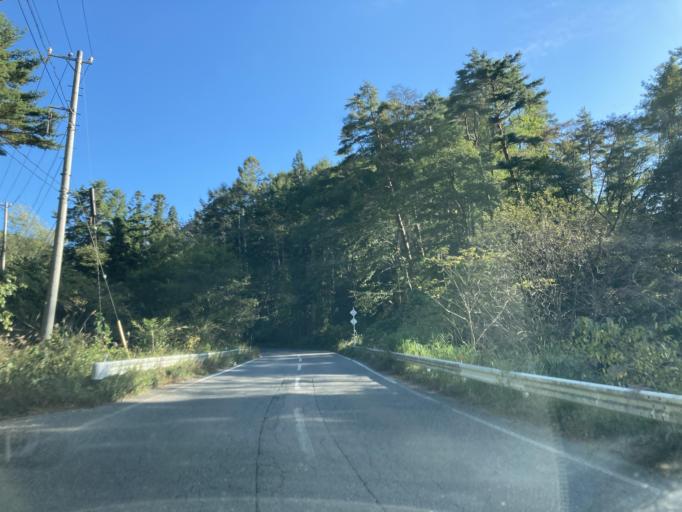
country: JP
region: Nagano
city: Omachi
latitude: 36.4899
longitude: 137.8819
